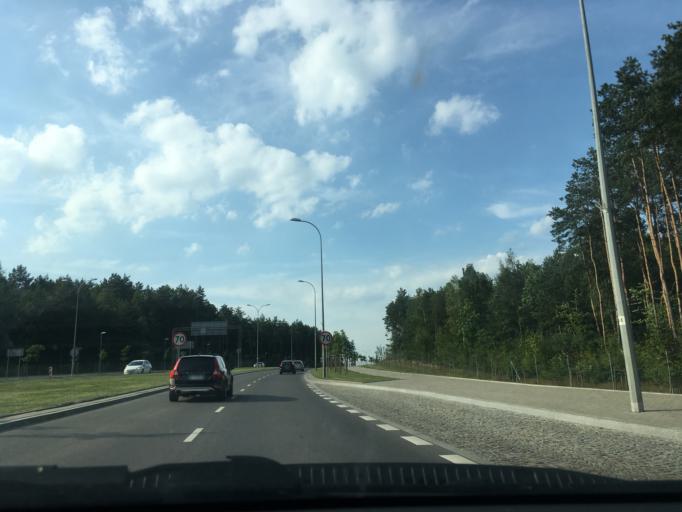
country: PL
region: Podlasie
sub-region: Bialystok
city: Bialystok
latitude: 53.1297
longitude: 23.2230
